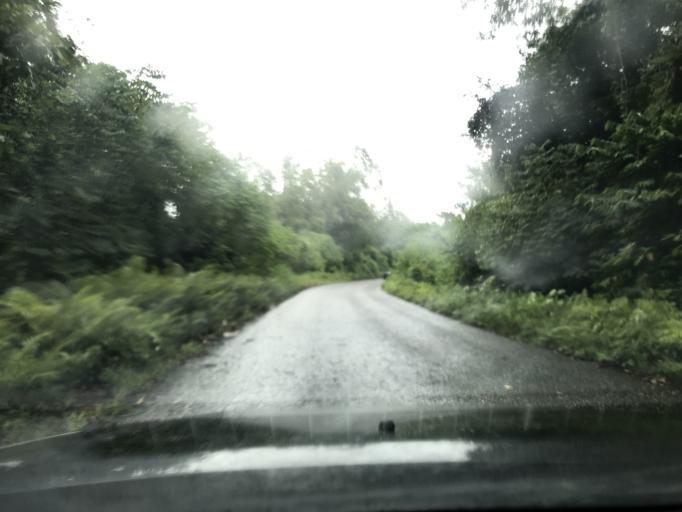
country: SB
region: Western Province
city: Gizo
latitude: -8.2666
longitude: 157.2357
